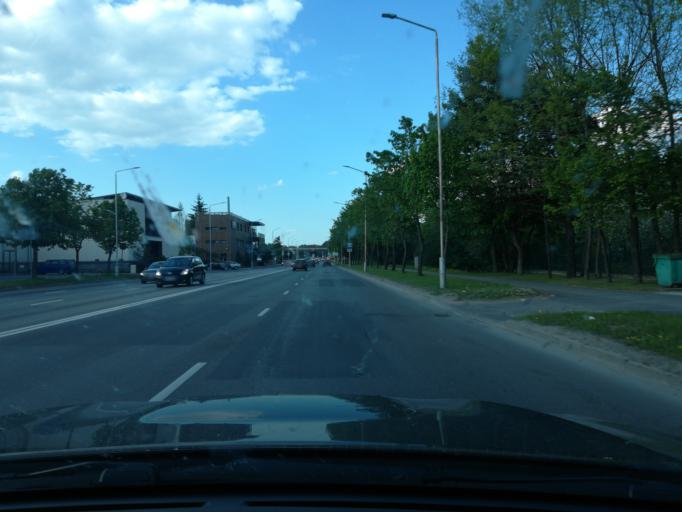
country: LT
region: Kauno apskritis
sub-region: Kaunas
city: Eiguliai
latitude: 54.9315
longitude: 23.9172
